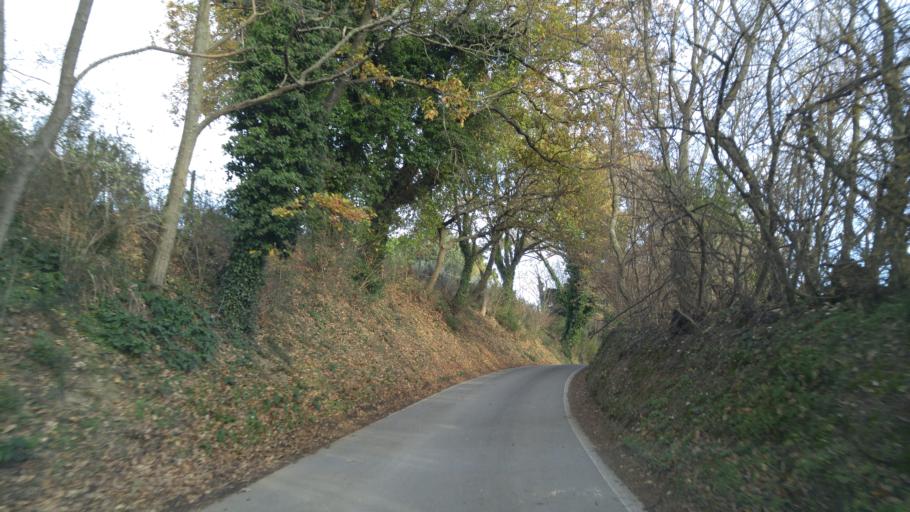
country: IT
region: The Marches
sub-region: Provincia di Pesaro e Urbino
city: Fenile
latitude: 43.8266
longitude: 12.9410
